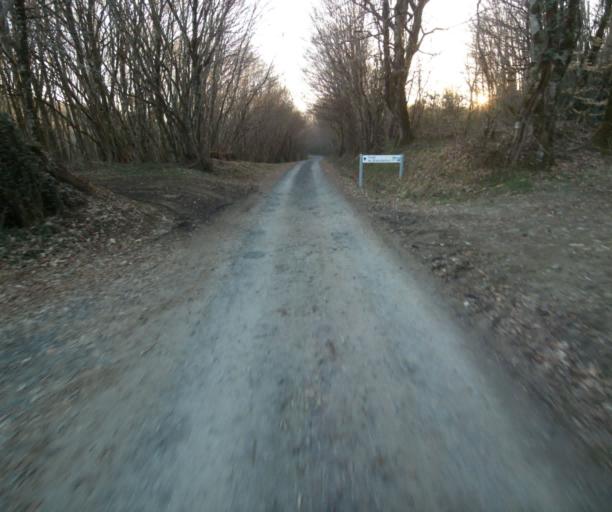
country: FR
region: Limousin
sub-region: Departement de la Correze
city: Uzerche
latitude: 45.3555
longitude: 1.6049
